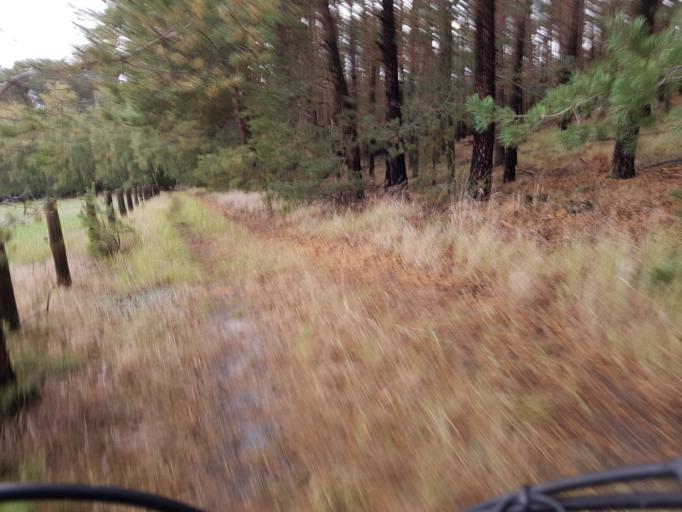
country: DE
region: Brandenburg
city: Schilda
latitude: 51.6153
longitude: 13.3857
